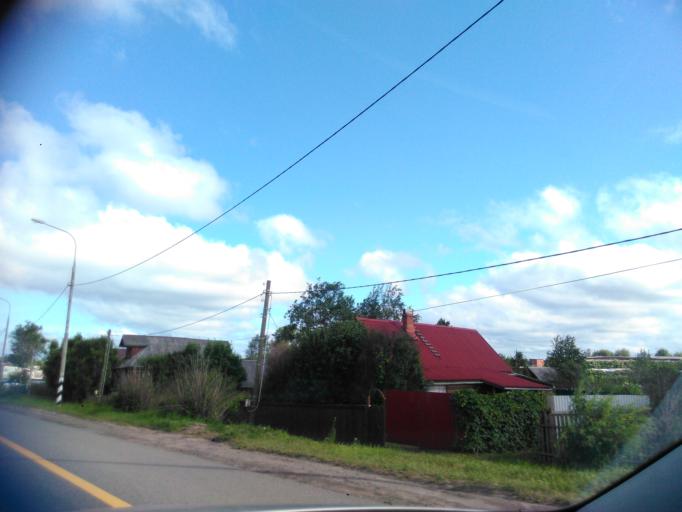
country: RU
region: Moskovskaya
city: Klin
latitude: 56.2824
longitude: 36.8243
